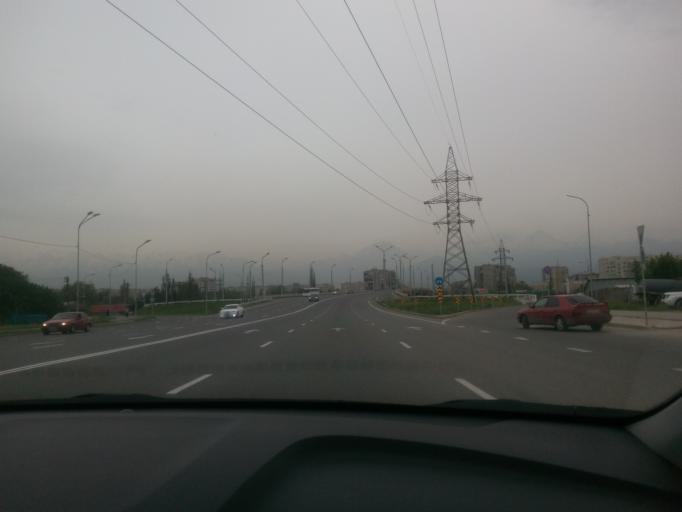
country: KZ
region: Almaty Qalasy
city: Almaty
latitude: 43.2462
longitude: 76.8265
